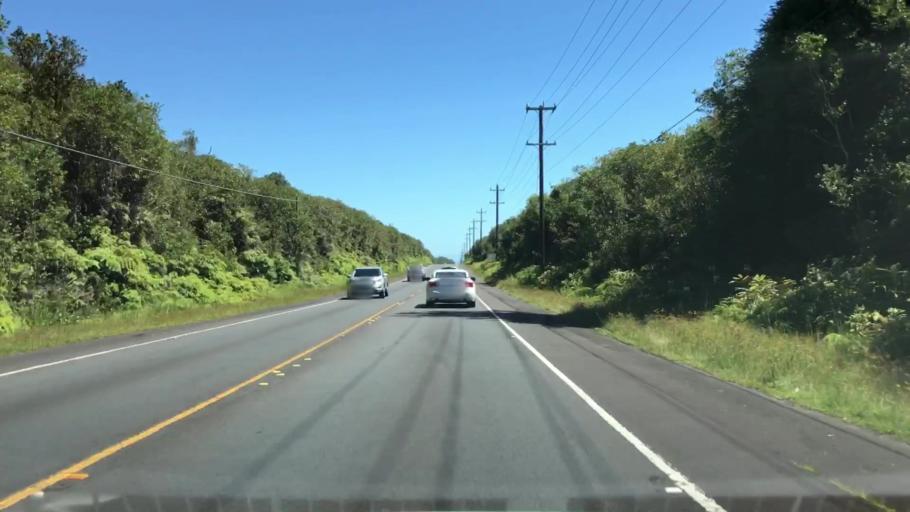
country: US
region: Hawaii
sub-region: Hawaii County
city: Volcano
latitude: 19.4586
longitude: -155.1709
